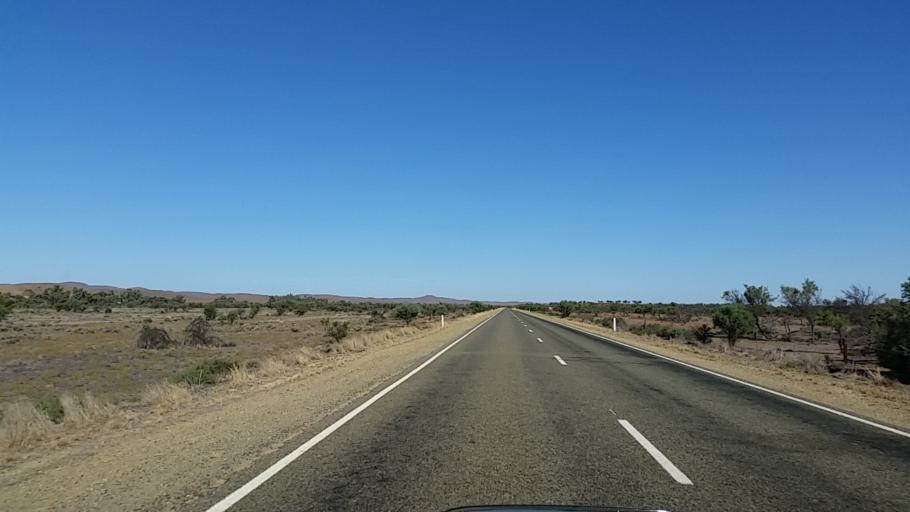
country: AU
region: South Australia
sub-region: Flinders Ranges
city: Quorn
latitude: -32.3885
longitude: 138.5050
